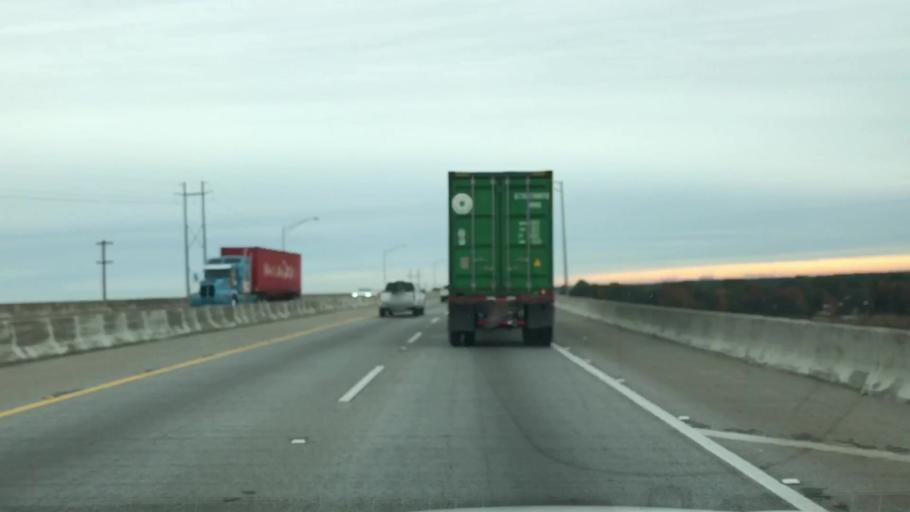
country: US
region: South Carolina
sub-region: Charleston County
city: North Charleston
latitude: 32.8871
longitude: -79.9425
